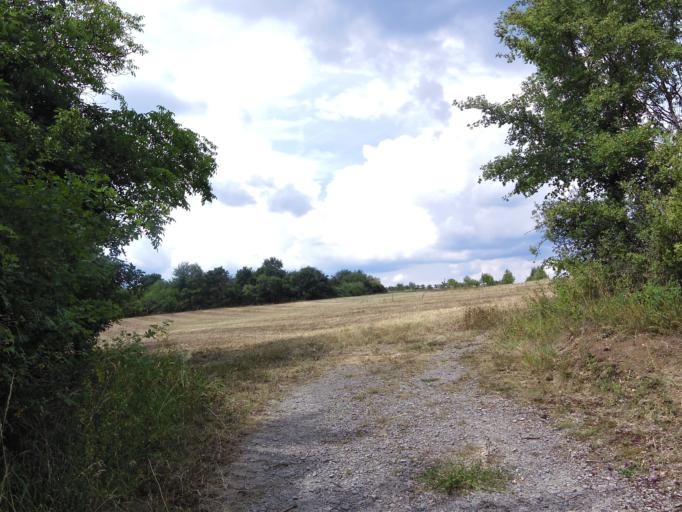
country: DE
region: Bavaria
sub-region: Regierungsbezirk Unterfranken
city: Randersacker
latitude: 49.7639
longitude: 9.9761
